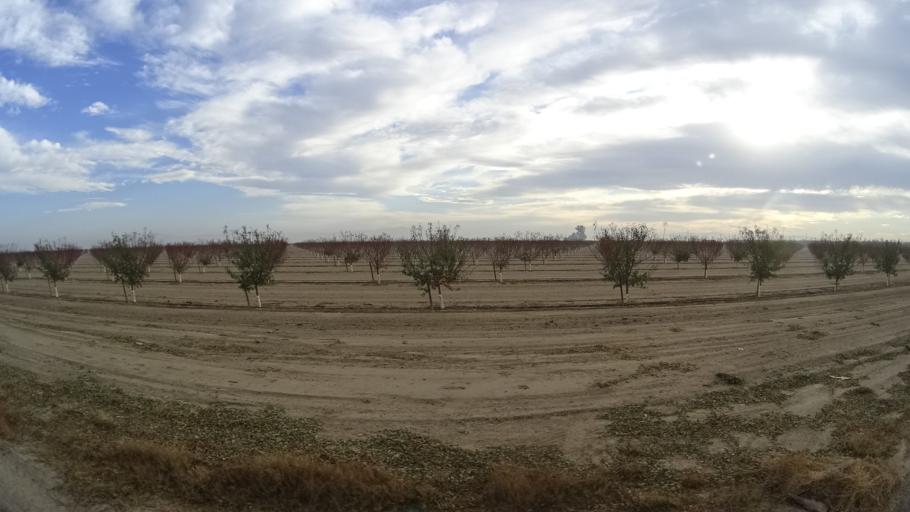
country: US
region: California
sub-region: Kern County
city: Rosedale
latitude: 35.4078
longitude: -119.1899
